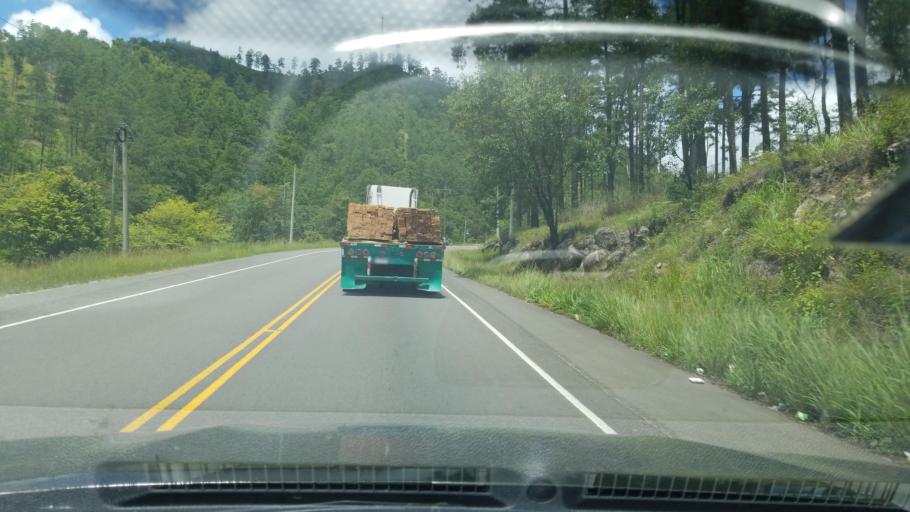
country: HN
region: Francisco Morazan
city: Talanga
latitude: 14.3939
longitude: -87.1287
